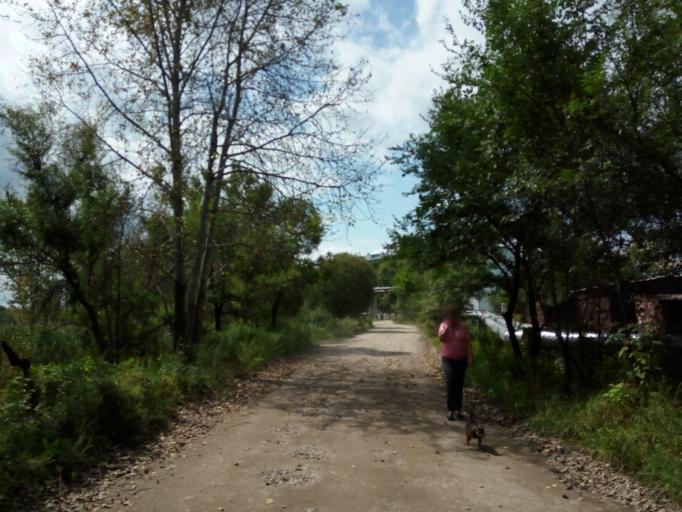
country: RU
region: Primorskiy
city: Dal'nerechensk
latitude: 45.9442
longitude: 133.8173
